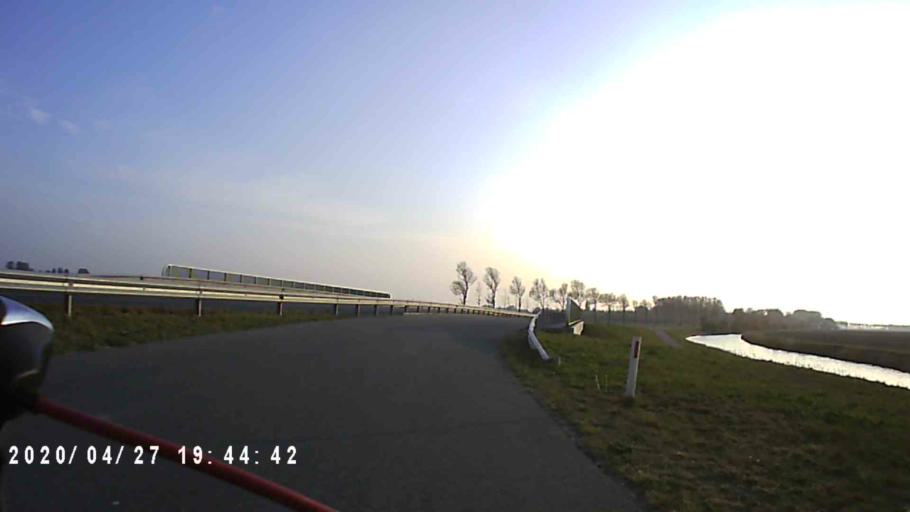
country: NL
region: Groningen
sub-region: Gemeente Winsum
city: Winsum
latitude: 53.3514
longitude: 6.4599
